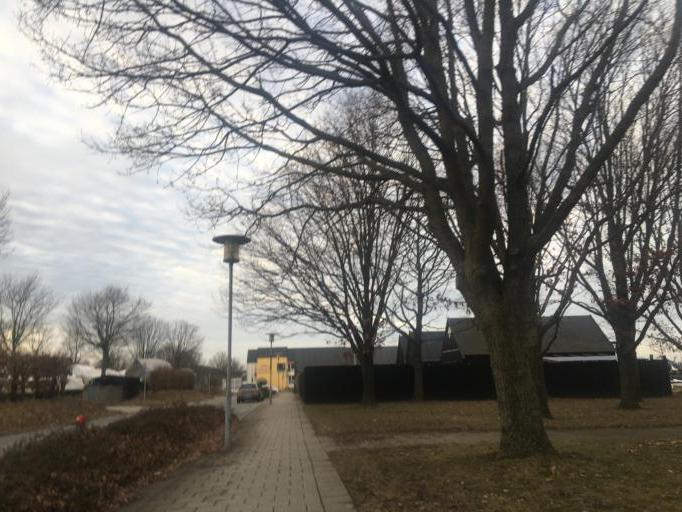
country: DK
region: Capital Region
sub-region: Dragor Kommune
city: Dragor
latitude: 55.6395
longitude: 12.6535
